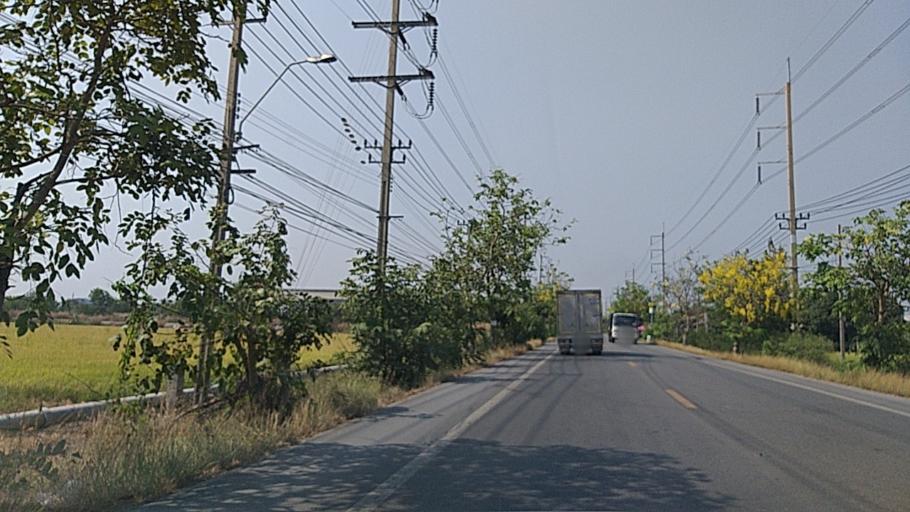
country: TH
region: Nonthaburi
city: Sai Noi
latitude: 14.0351
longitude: 100.3122
